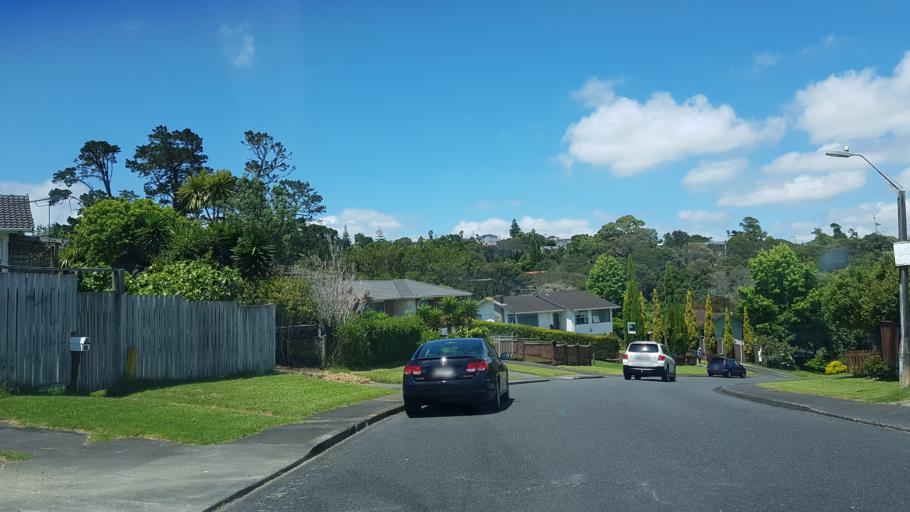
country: NZ
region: Auckland
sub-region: Auckland
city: North Shore
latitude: -36.7852
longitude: 174.7186
